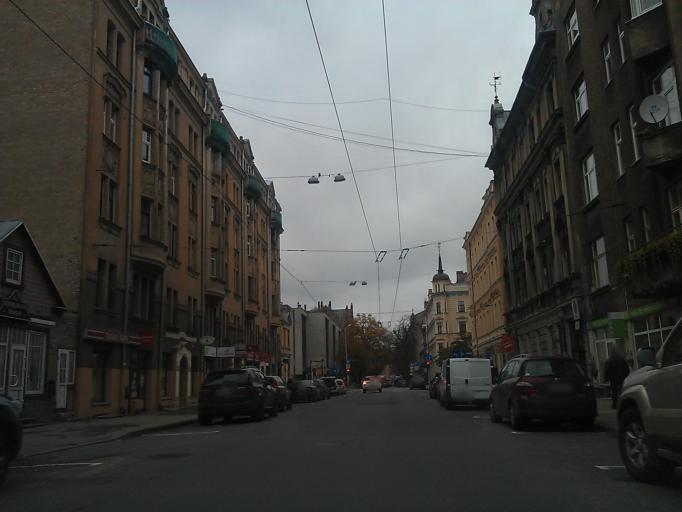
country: LV
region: Riga
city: Riga
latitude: 56.9556
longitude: 24.1329
